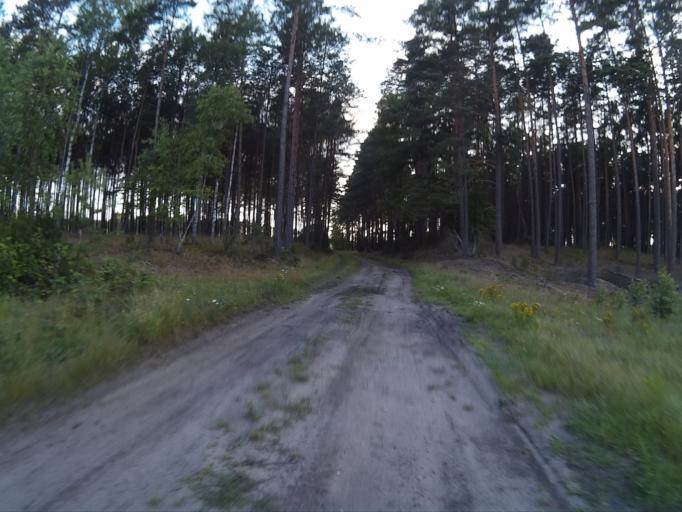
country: PL
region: Kujawsko-Pomorskie
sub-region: Powiat swiecki
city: Lniano
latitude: 53.5509
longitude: 18.1681
